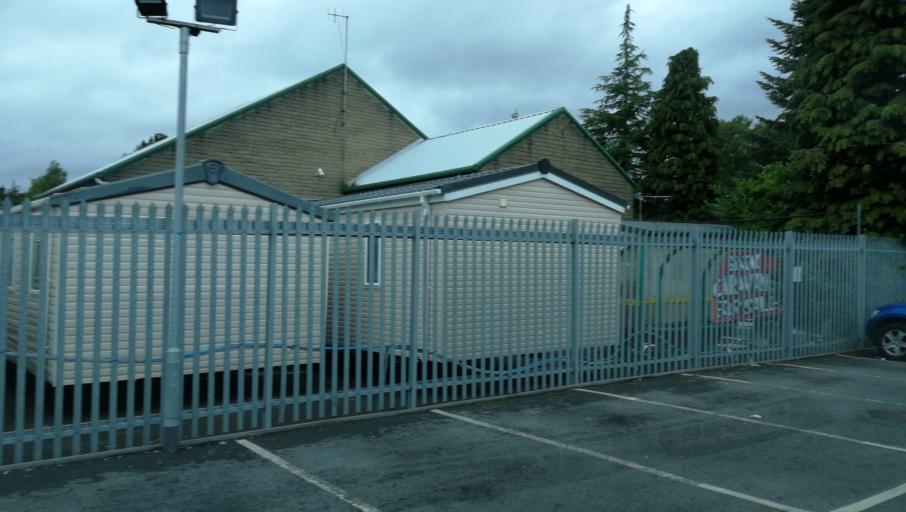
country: GB
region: England
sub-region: Borough of Tameside
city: Longdendale
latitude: 53.4540
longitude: -1.9847
